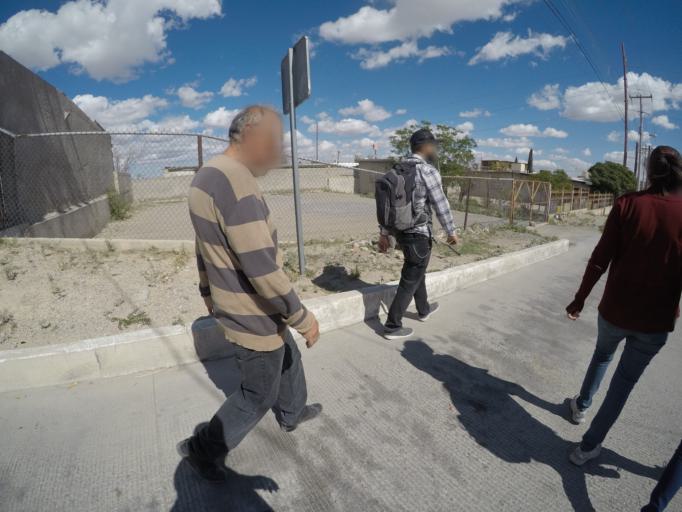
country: MX
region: Chihuahua
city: Ciudad Juarez
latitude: 31.6923
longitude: -106.4816
